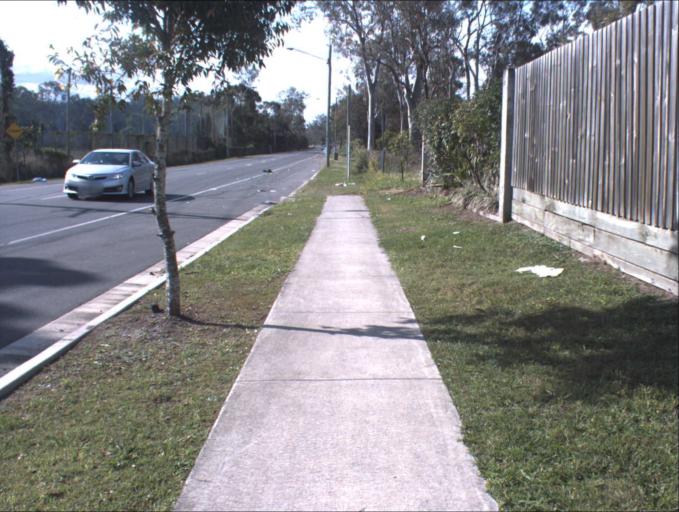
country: AU
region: Queensland
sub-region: Logan
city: Logan City
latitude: -27.6686
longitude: 153.0911
